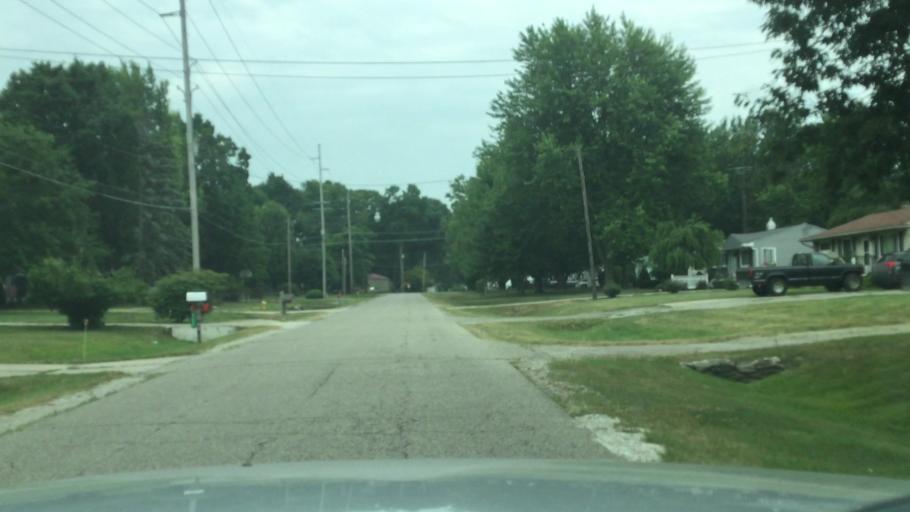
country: US
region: Michigan
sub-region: Genesee County
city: Flint
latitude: 42.9686
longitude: -83.7028
